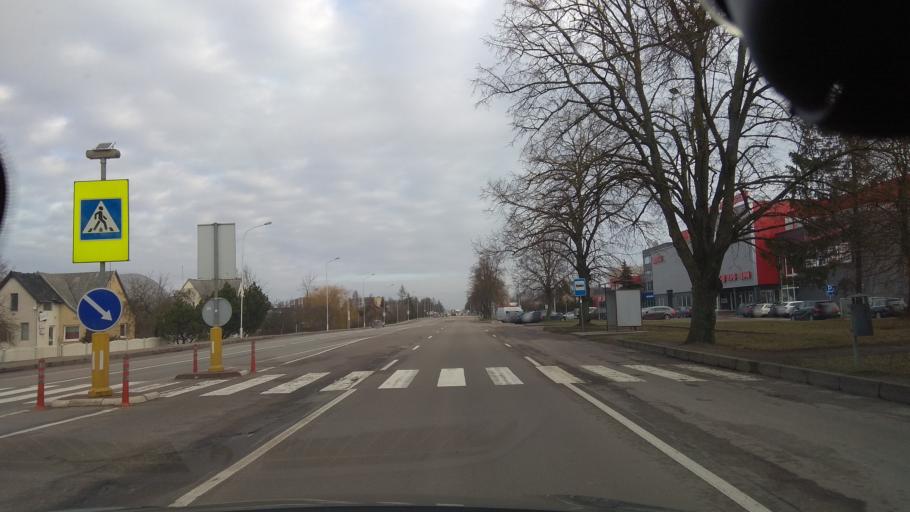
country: LT
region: Marijampoles apskritis
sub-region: Marijampole Municipality
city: Marijampole
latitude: 54.5733
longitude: 23.3671
